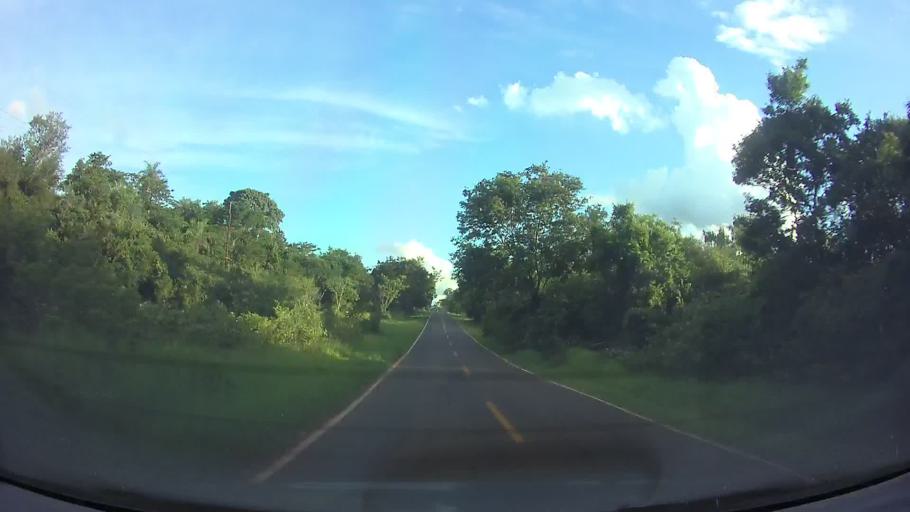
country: PY
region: Paraguari
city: Acahay
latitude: -25.9568
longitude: -57.0906
